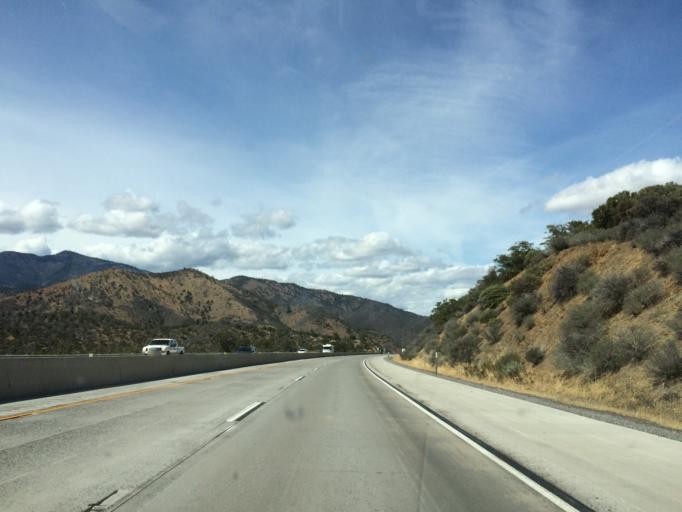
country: US
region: California
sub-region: Siskiyou County
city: Yreka
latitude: 41.8192
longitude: -122.5776
